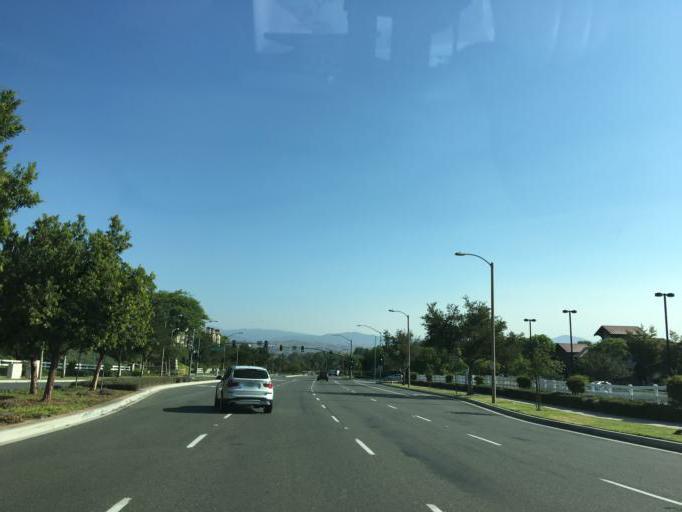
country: US
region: California
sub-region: Los Angeles County
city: Santa Clarita
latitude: 34.4087
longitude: -118.5796
